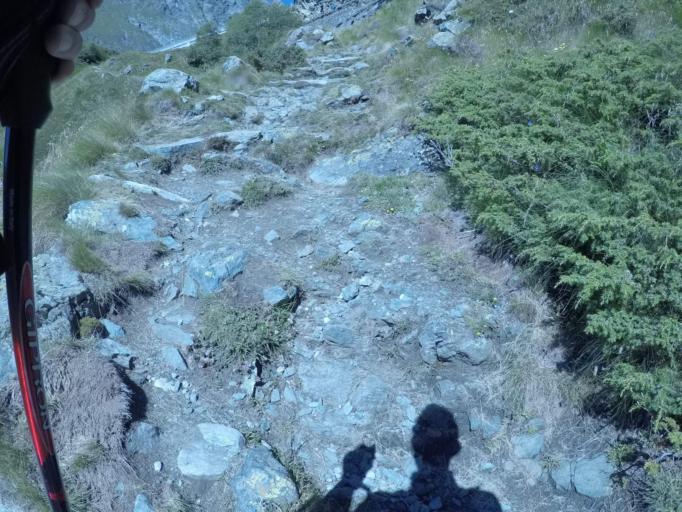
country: IT
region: Aosta Valley
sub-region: Valle d'Aosta
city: Valtournenche
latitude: 45.8794
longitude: 7.5974
